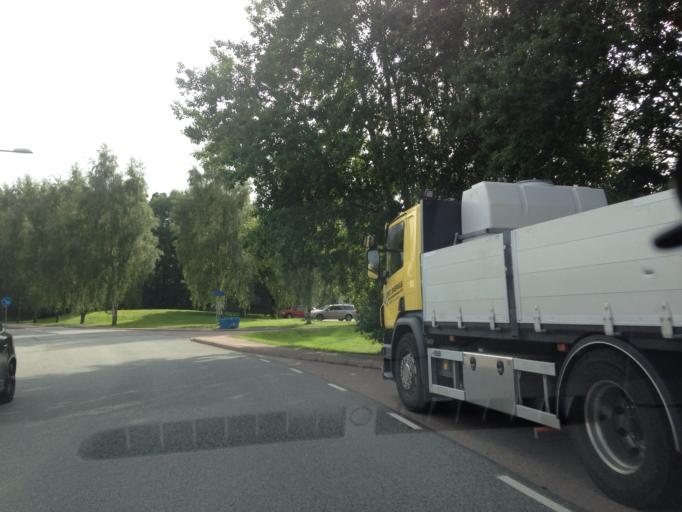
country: SE
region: Vaestra Goetaland
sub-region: Goteborg
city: Goeteborg
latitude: 57.7633
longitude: 11.9705
